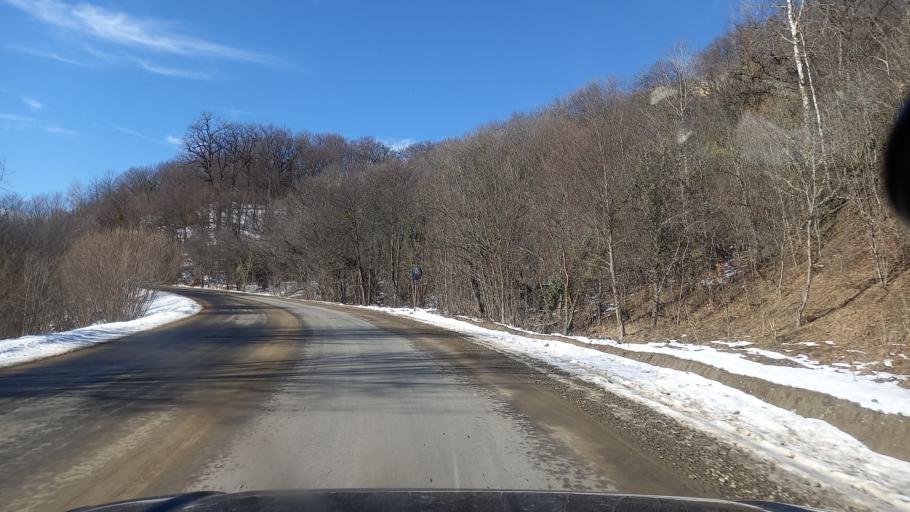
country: RU
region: Adygeya
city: Kamennomostskiy
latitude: 44.2400
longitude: 40.1728
